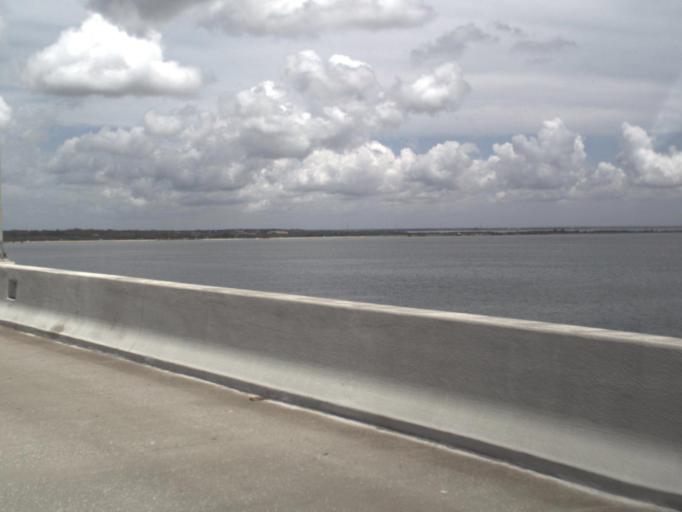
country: US
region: Florida
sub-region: Pinellas County
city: South Highpoint
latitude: 27.9436
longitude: -82.7043
